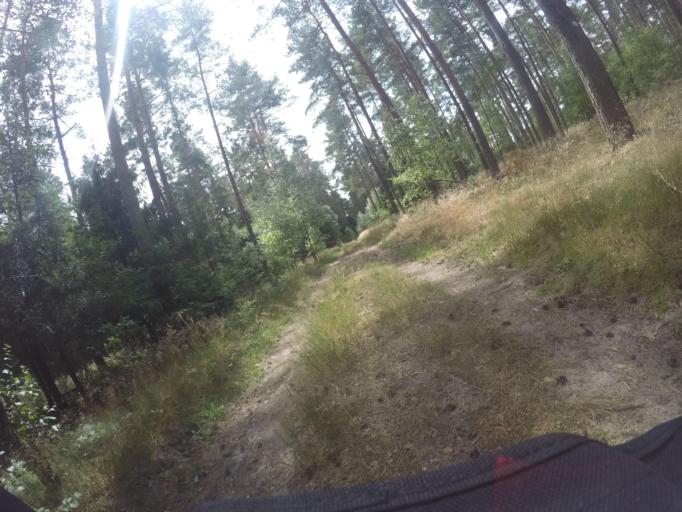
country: DE
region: Lower Saxony
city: Dahlem
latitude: 53.2346
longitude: 10.7256
